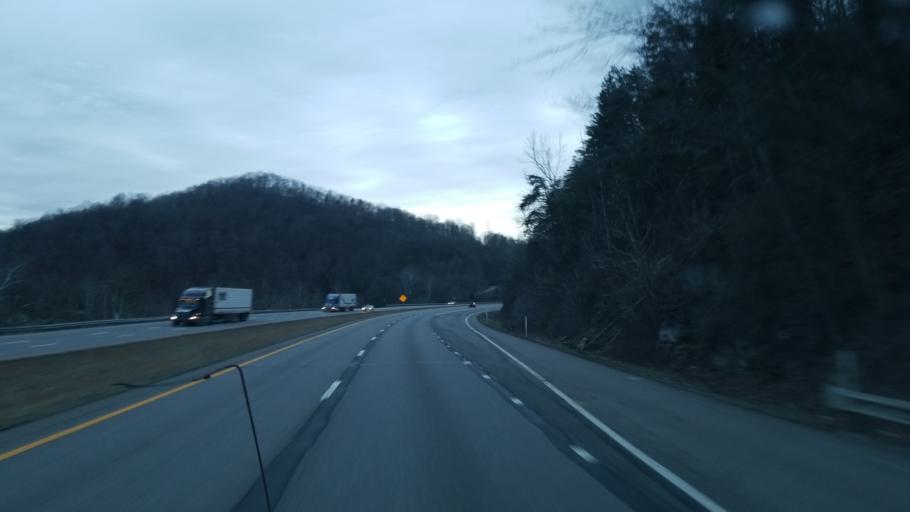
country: US
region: West Virginia
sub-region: Kanawha County
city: Sissonville
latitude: 38.5488
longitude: -81.6349
